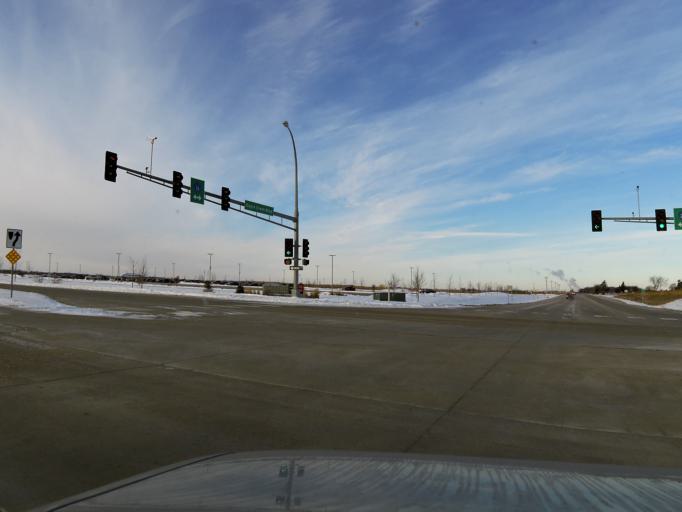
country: US
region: Minnesota
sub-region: Scott County
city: Prior Lake
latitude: 44.7675
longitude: -93.4358
